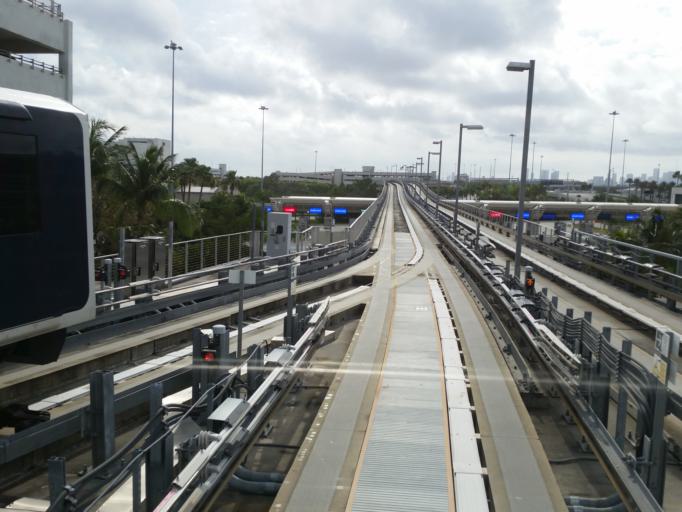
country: US
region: Florida
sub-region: Miami-Dade County
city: Miami Springs
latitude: 25.7952
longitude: -80.2754
